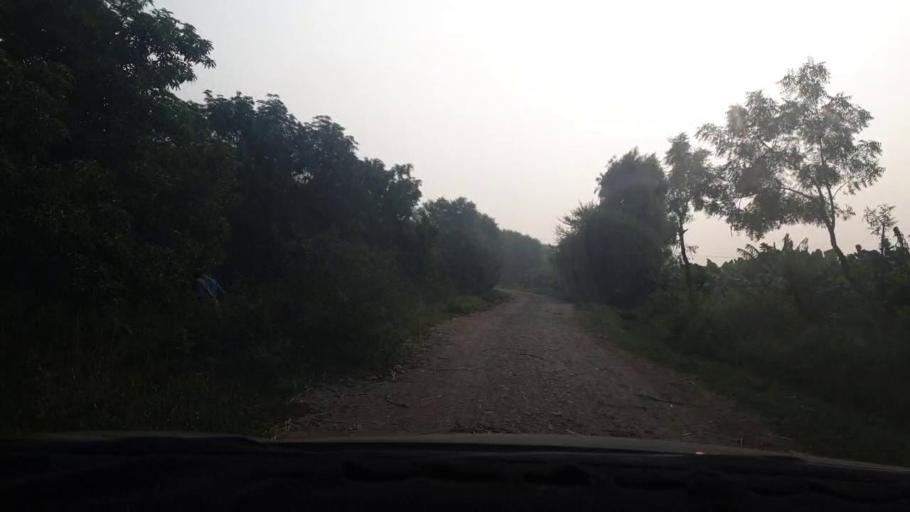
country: PK
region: Sindh
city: Matiari
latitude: 25.5840
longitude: 68.4549
